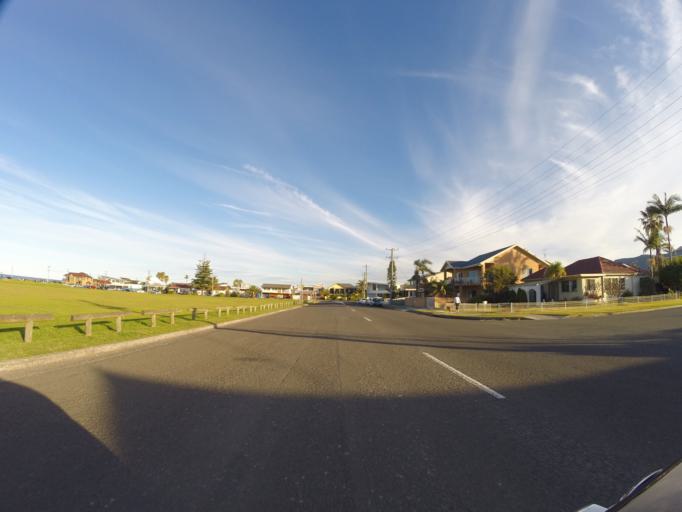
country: AU
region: New South Wales
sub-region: Wollongong
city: Bulli
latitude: -34.3488
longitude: 150.9179
